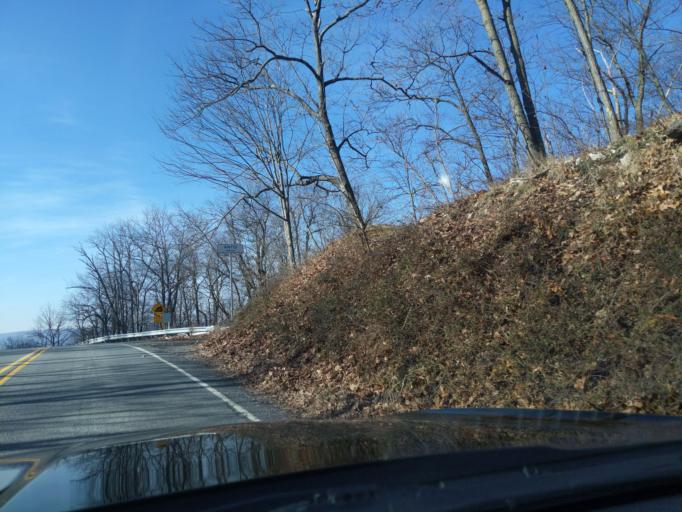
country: US
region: Pennsylvania
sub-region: Blair County
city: Tipton
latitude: 40.6214
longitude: -78.2812
